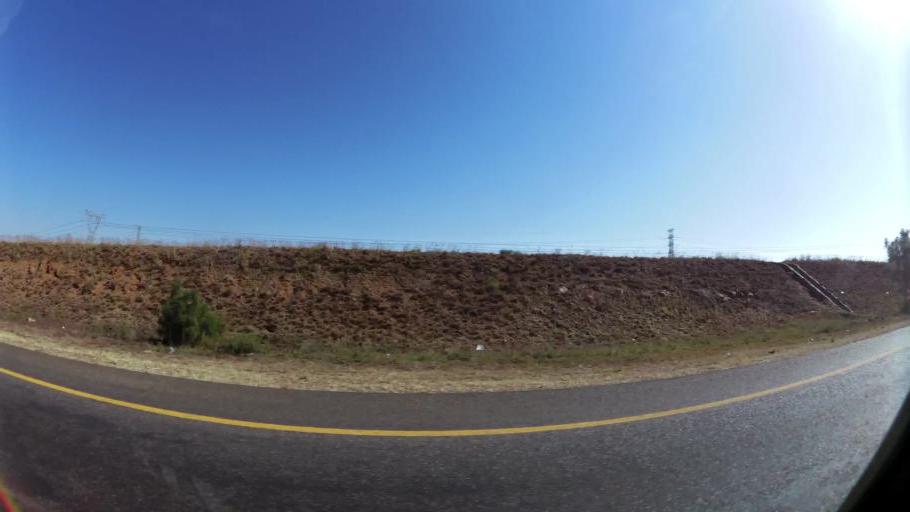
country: ZA
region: Gauteng
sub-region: City of Tshwane Metropolitan Municipality
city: Mabopane
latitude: -25.5476
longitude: 28.1102
